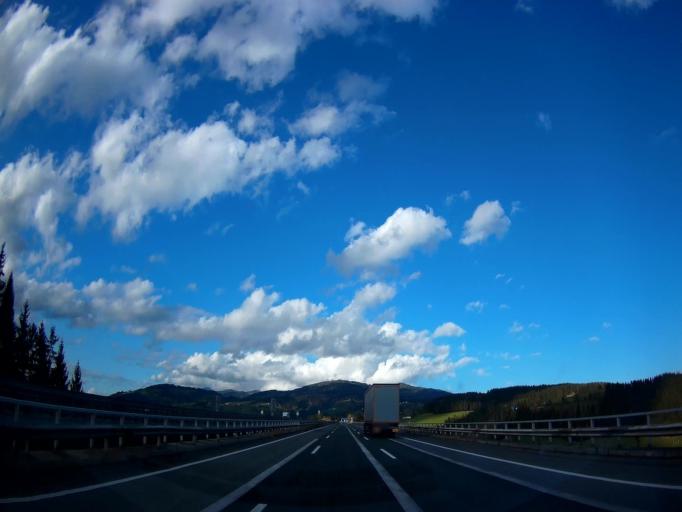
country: AT
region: Carinthia
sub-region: Politischer Bezirk Wolfsberg
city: Bad Sankt Leonhard im Lavanttal
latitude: 46.9179
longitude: 14.8390
